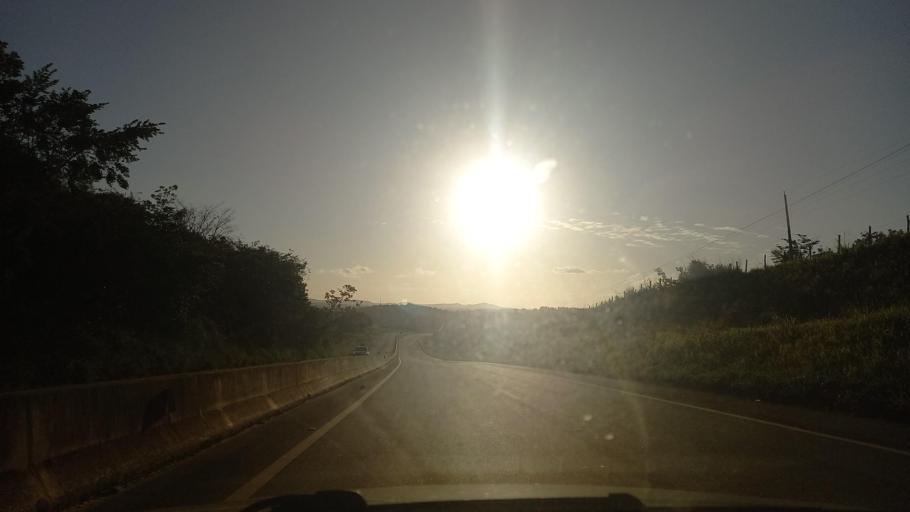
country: BR
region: Alagoas
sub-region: Limoeiro De Anadia
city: Limoeiro de Anadia
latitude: -9.7403
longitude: -36.4801
